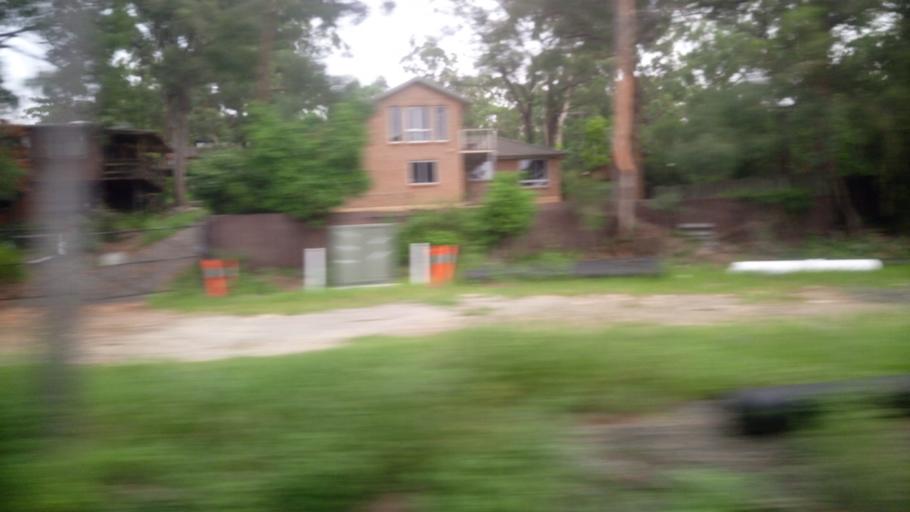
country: AU
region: New South Wales
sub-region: Blue Mountains Municipality
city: Glenbrook
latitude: -33.7765
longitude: 150.6423
